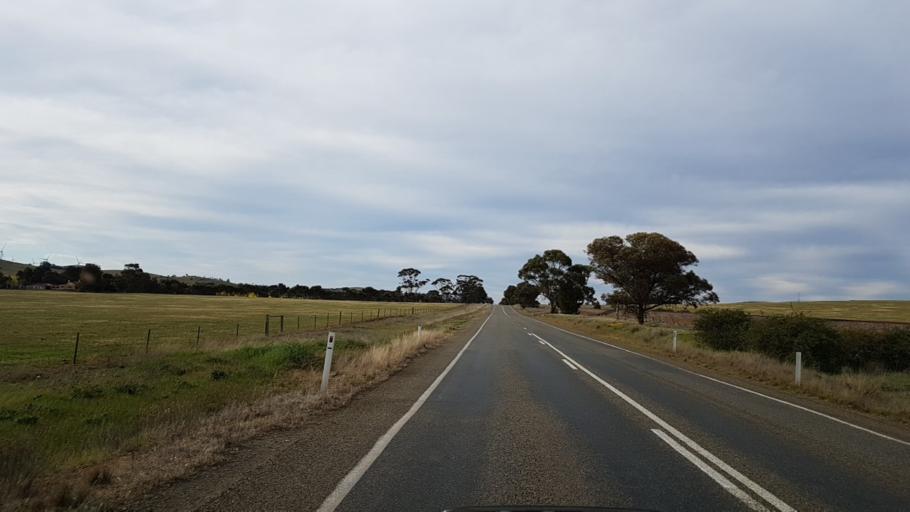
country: AU
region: South Australia
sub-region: Northern Areas
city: Jamestown
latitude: -33.1591
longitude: 138.6140
